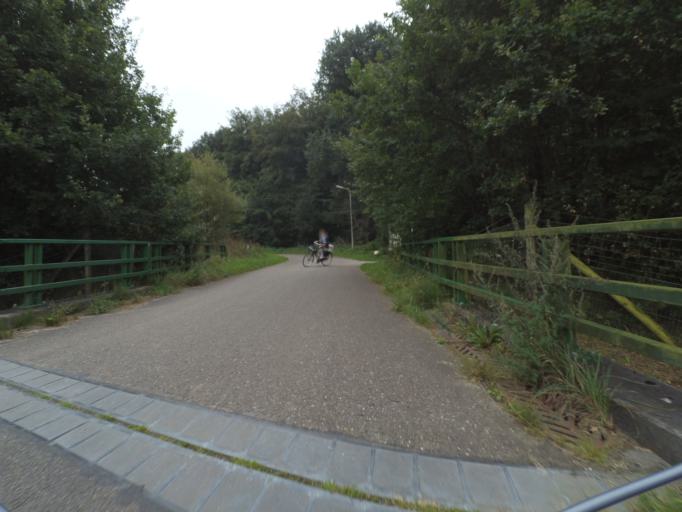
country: NL
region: Overijssel
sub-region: Gemeente Oldenzaal
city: Oldenzaal
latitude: 52.3053
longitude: 6.9791
